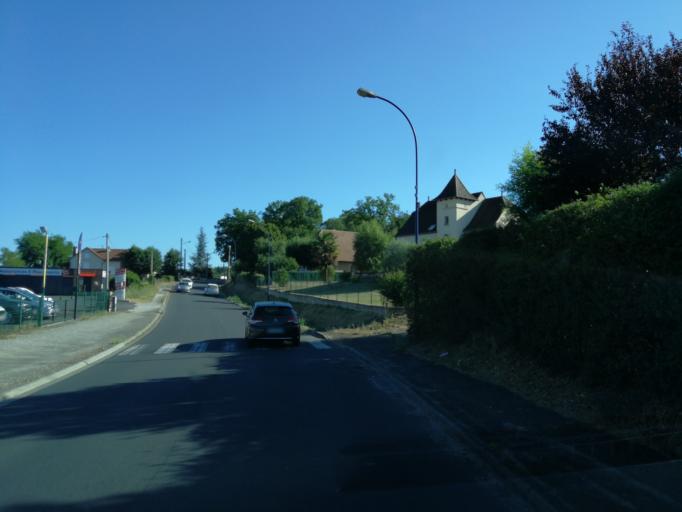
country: FR
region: Midi-Pyrenees
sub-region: Departement du Lot
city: Gourdon
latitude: 44.7307
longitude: 1.3739
